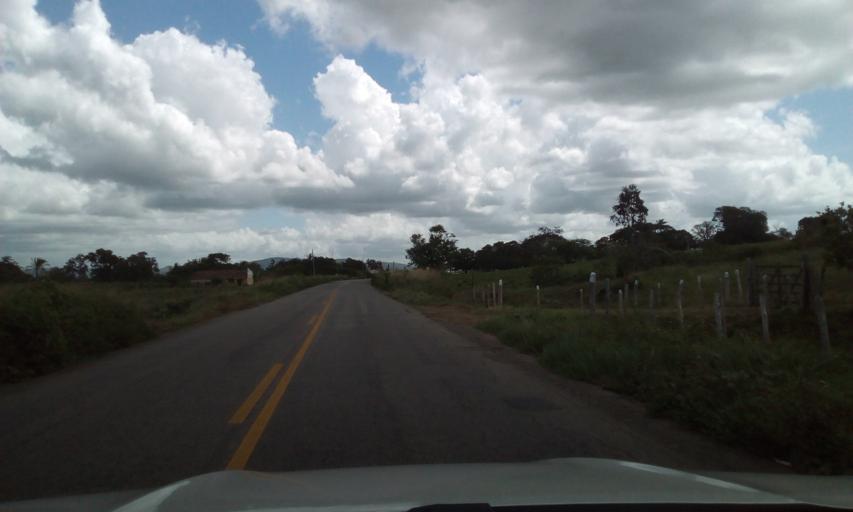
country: BR
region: Paraiba
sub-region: Guarabira
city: Guarabira
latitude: -6.8588
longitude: -35.4316
